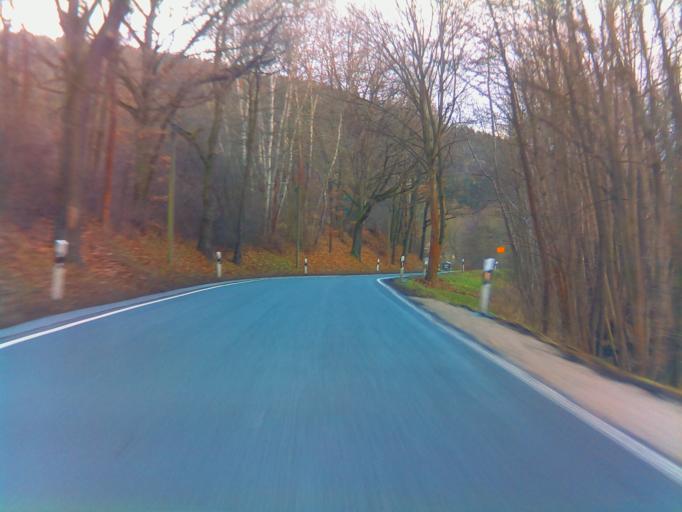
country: DE
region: Thuringia
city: Rottenbach
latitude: 50.6979
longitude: 11.1319
